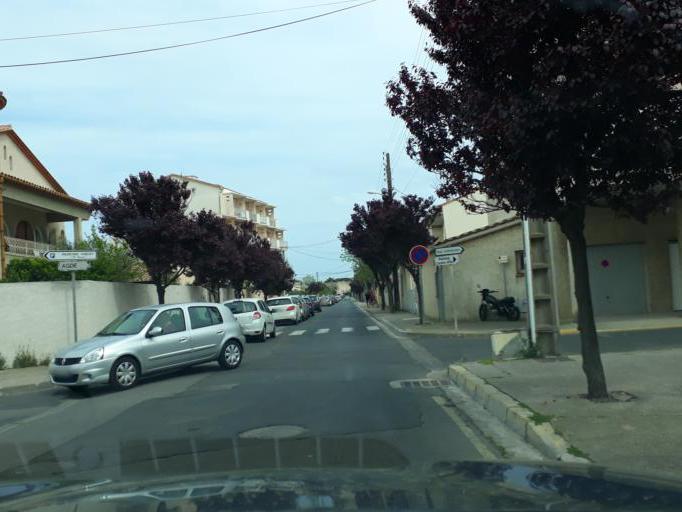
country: FR
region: Languedoc-Roussillon
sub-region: Departement de l'Herault
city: Agde
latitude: 43.2843
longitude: 3.4495
